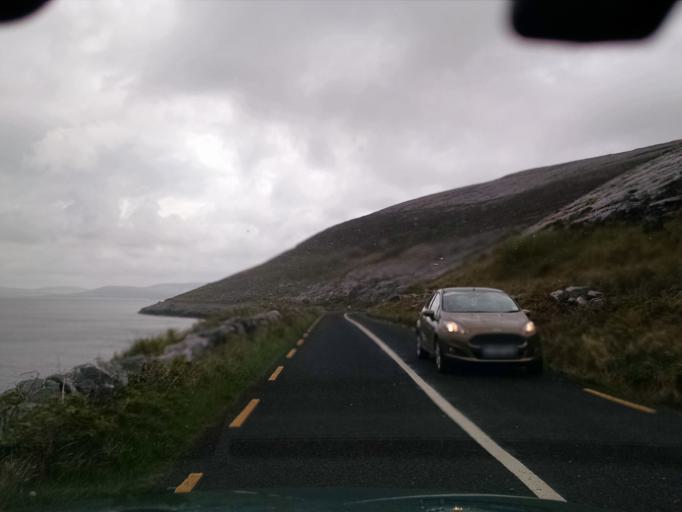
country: IE
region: Connaught
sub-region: County Galway
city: Bearna
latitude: 53.1528
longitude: -9.2595
